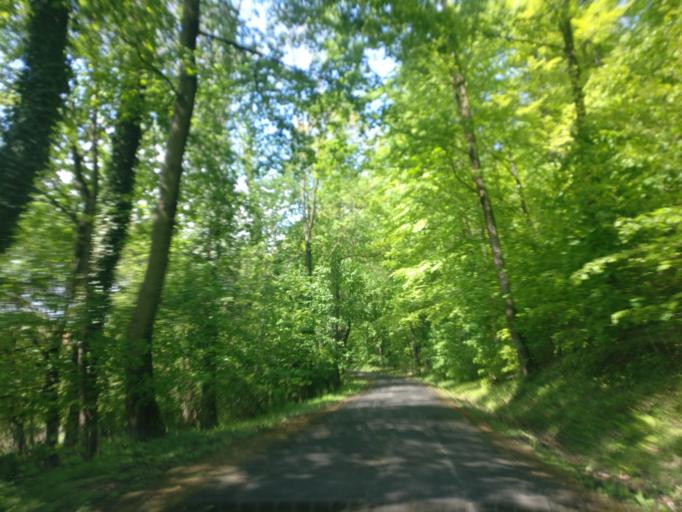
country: DE
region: Lower Saxony
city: Hannoversch Munden
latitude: 51.4501
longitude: 9.6490
